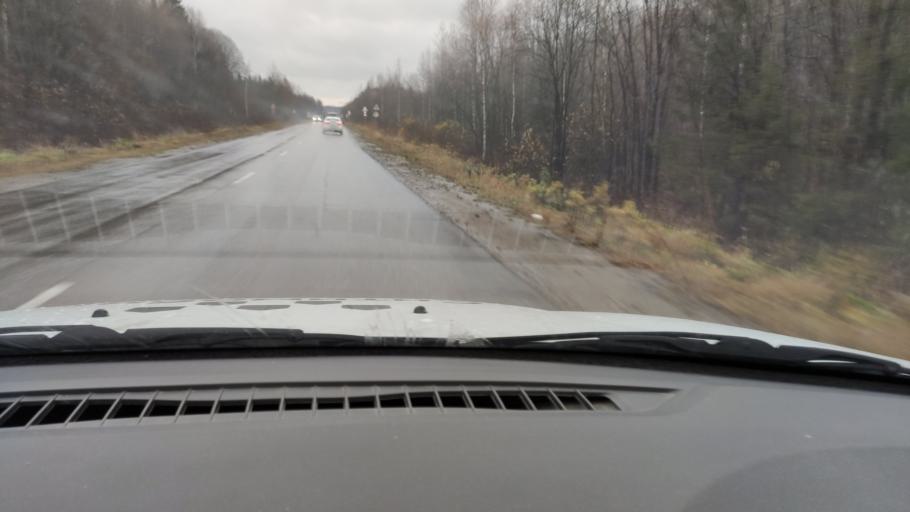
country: RU
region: Perm
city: Novyye Lyady
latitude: 58.0288
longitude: 56.6234
